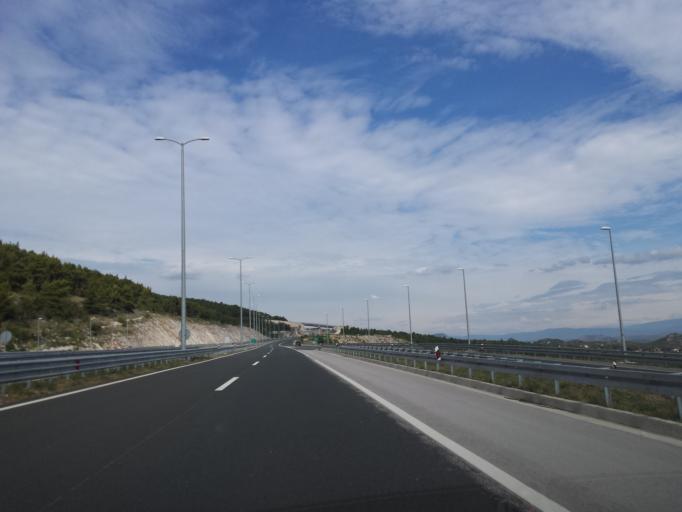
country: BA
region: Federation of Bosnia and Herzegovina
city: Ljubuski
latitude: 43.1493
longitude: 17.4841
